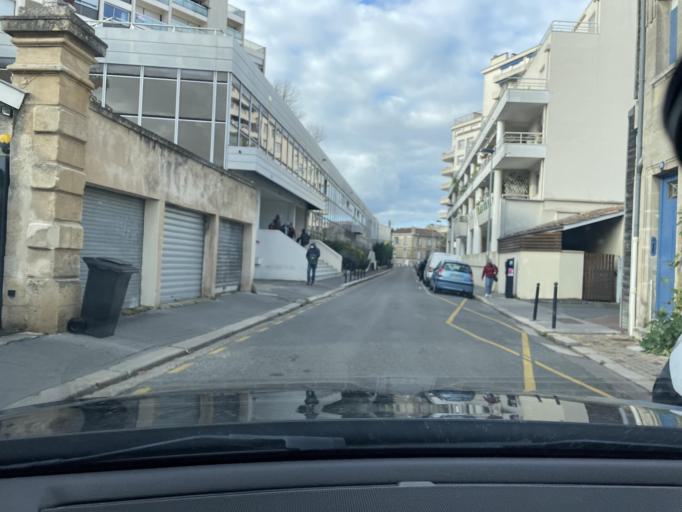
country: FR
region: Aquitaine
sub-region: Departement de la Gironde
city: Bordeaux
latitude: 44.8436
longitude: -0.5954
